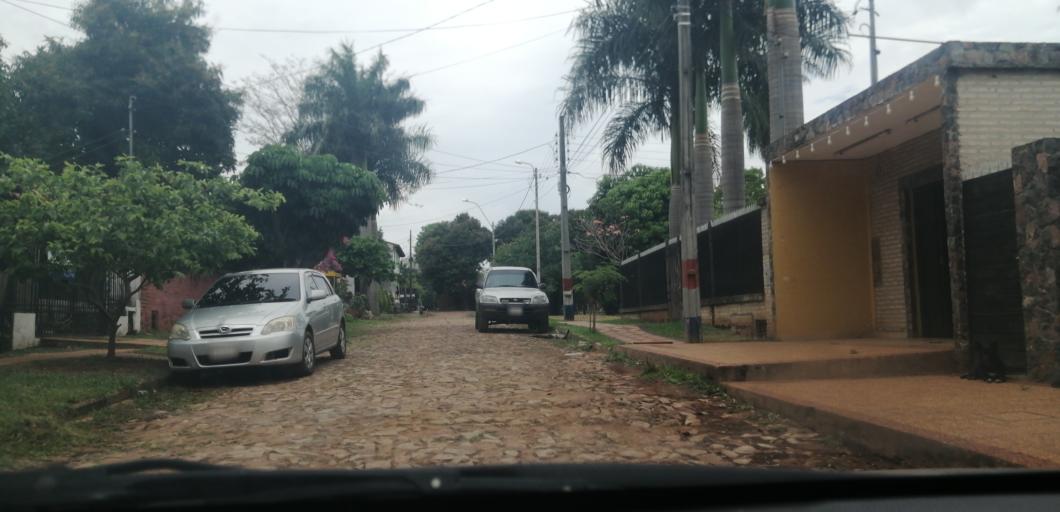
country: PY
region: Central
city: Colonia Mariano Roque Alonso
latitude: -25.1917
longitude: -57.5406
